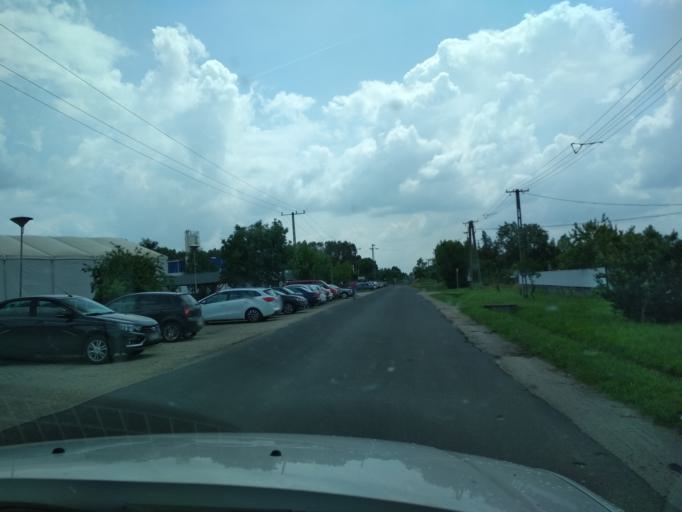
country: HU
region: Pest
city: Nagykata
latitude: 47.4000
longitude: 19.7596
